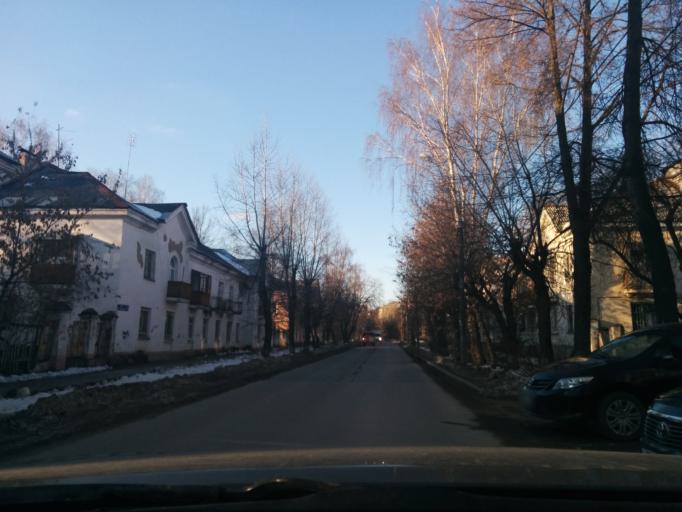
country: RU
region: Perm
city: Kultayevo
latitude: 58.0007
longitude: 55.9553
